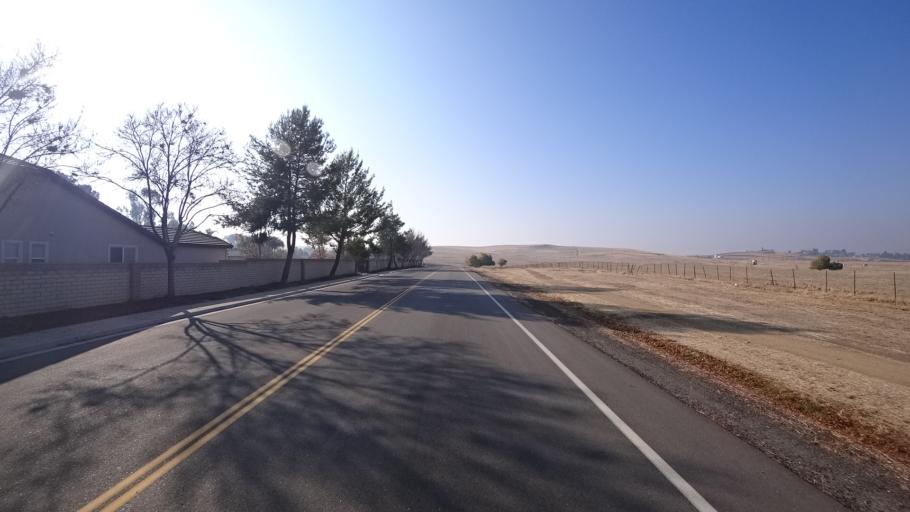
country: US
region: California
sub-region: Kern County
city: Lamont
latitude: 35.4038
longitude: -118.8445
